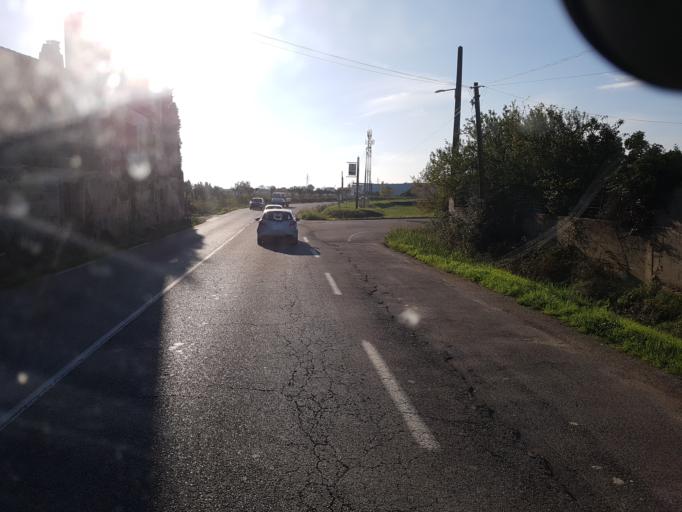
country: FR
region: Languedoc-Roussillon
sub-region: Departement du Gard
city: Redessan
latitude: 43.8263
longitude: 4.5017
